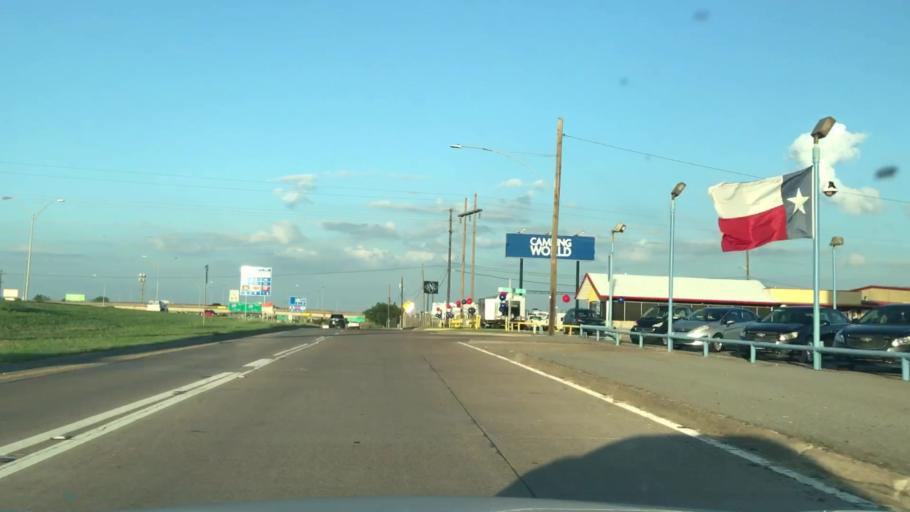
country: US
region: Texas
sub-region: Dallas County
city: Mesquite
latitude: 32.8160
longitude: -96.6413
